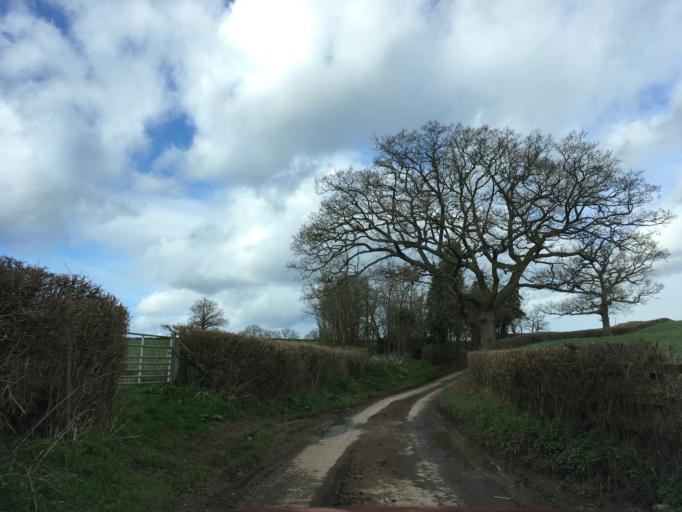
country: GB
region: England
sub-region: Gloucestershire
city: Newent
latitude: 51.8512
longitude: -2.3854
